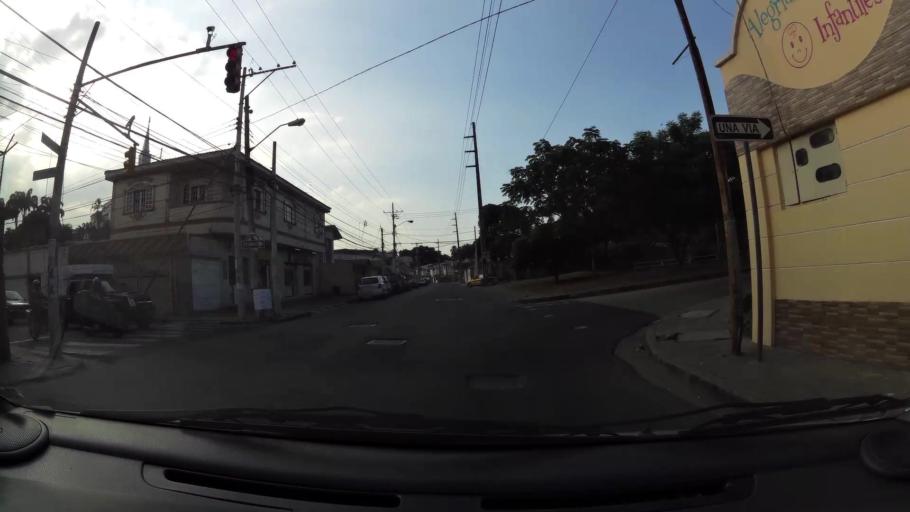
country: EC
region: Guayas
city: Guayaquil
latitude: -2.1575
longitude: -79.9038
